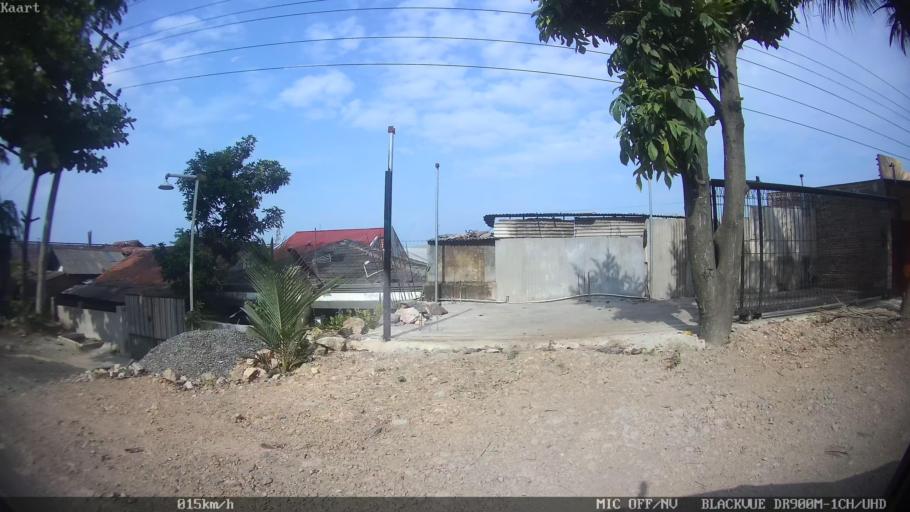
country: ID
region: Lampung
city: Panjang
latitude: -5.4717
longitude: 105.3244
